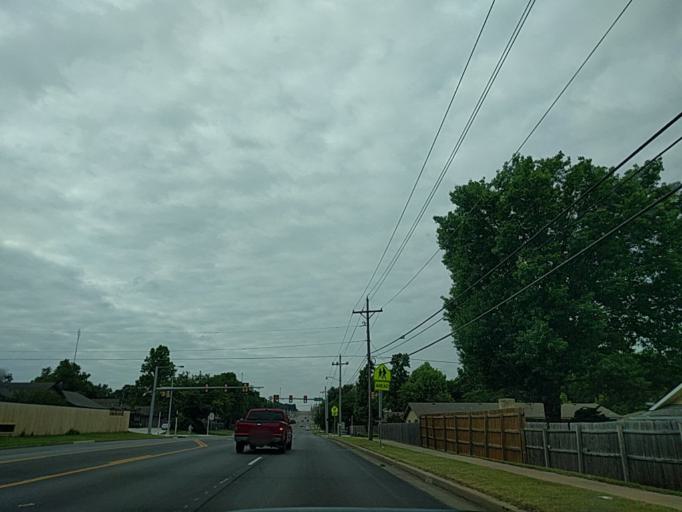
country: US
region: Oklahoma
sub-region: Tulsa County
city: Jenks
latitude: 36.0821
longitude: -95.9044
